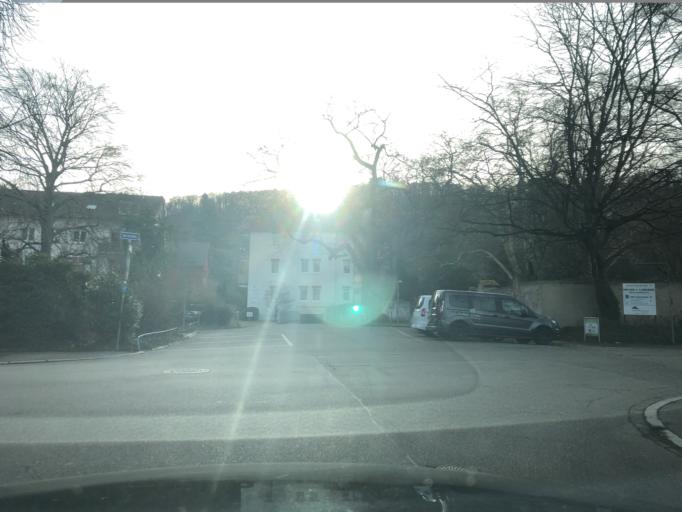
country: DE
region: Baden-Wuerttemberg
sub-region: Freiburg Region
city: Freiburg
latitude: 48.0017
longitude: 7.8566
